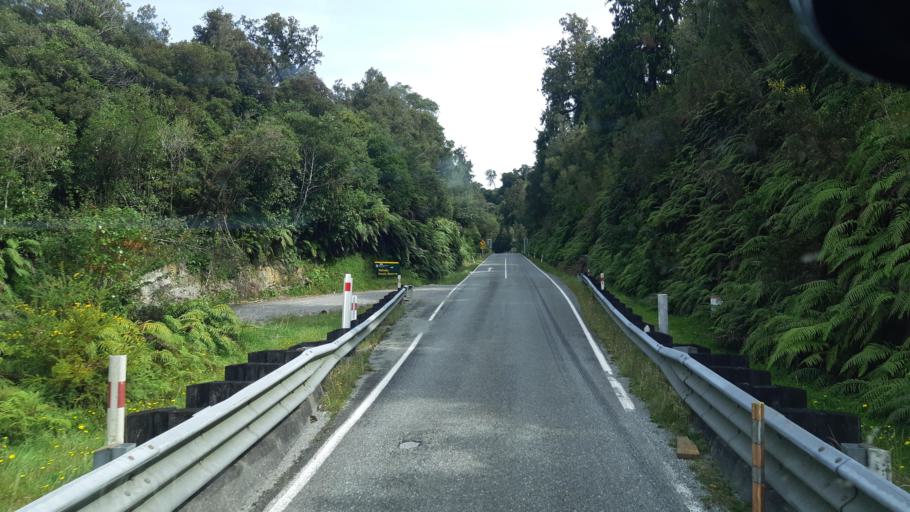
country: NZ
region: West Coast
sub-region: Westland District
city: Hokitika
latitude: -42.9809
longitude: 170.6841
